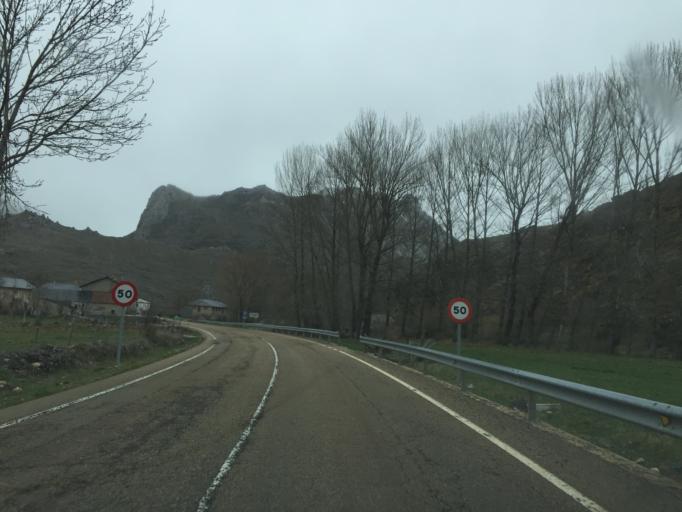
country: ES
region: Castille and Leon
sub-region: Provincia de Leon
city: San Emiliano
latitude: 42.9422
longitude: -5.9857
